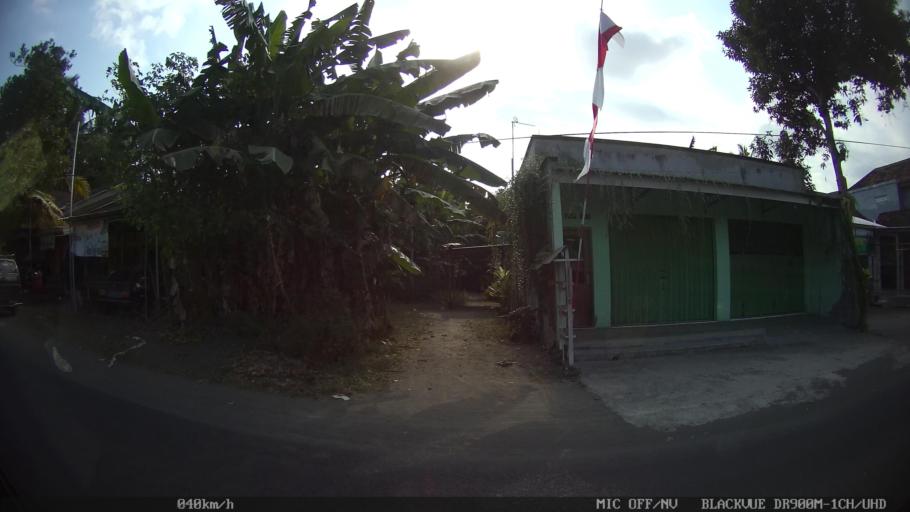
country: ID
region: Daerah Istimewa Yogyakarta
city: Bantul
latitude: -7.8661
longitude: 110.3187
